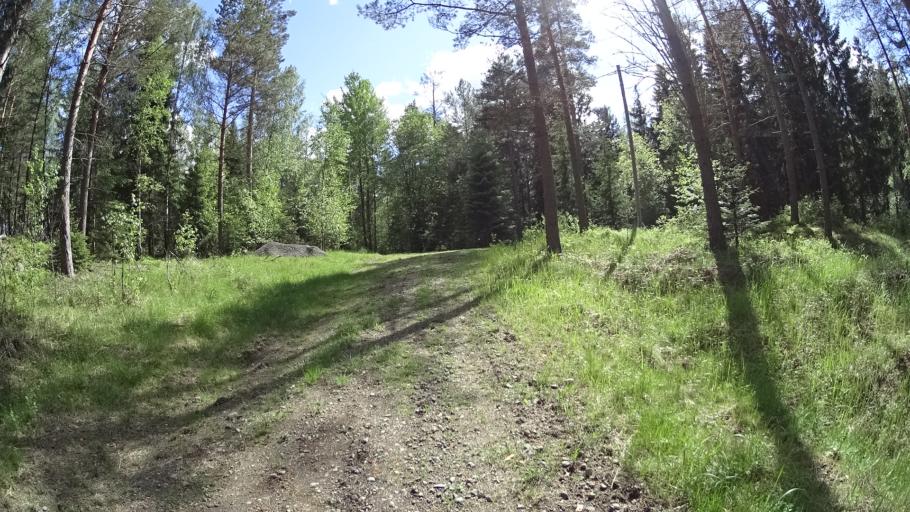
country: FI
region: Uusimaa
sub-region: Raaseporin
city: Pohja
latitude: 60.1826
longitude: 23.5850
